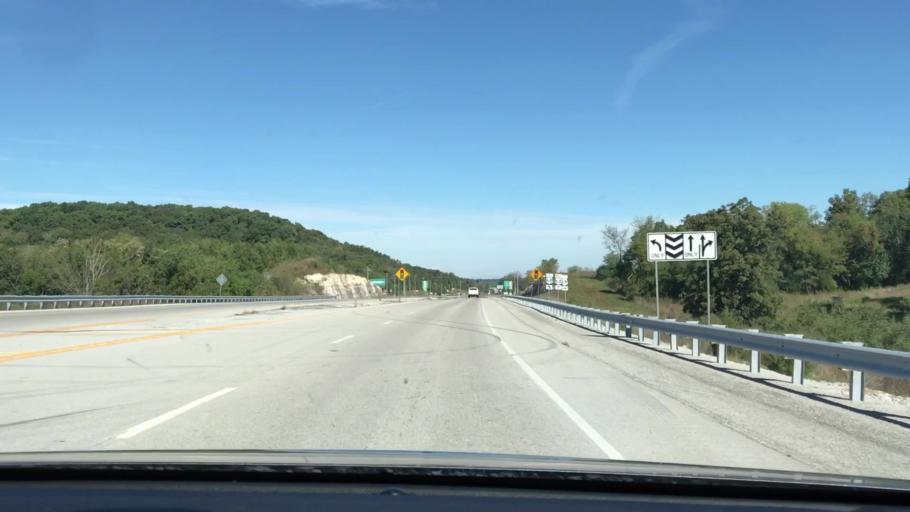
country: US
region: Kentucky
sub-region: Logan County
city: Russellville
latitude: 36.8387
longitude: -86.8634
